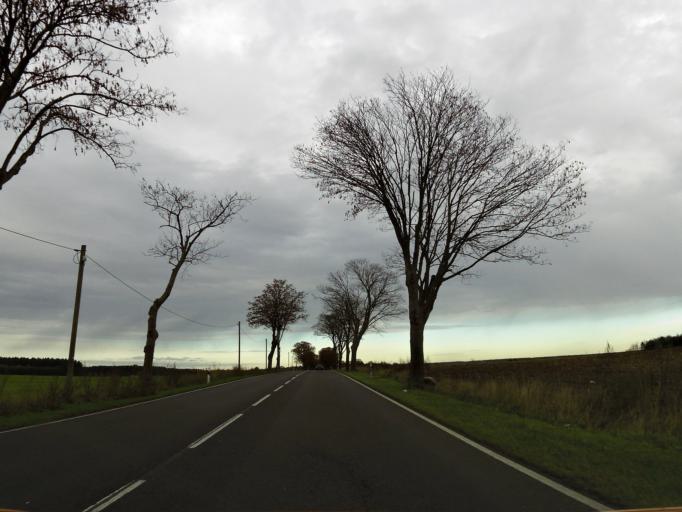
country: DE
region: Saxony-Anhalt
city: Letzlingen
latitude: 52.4302
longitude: 11.4827
